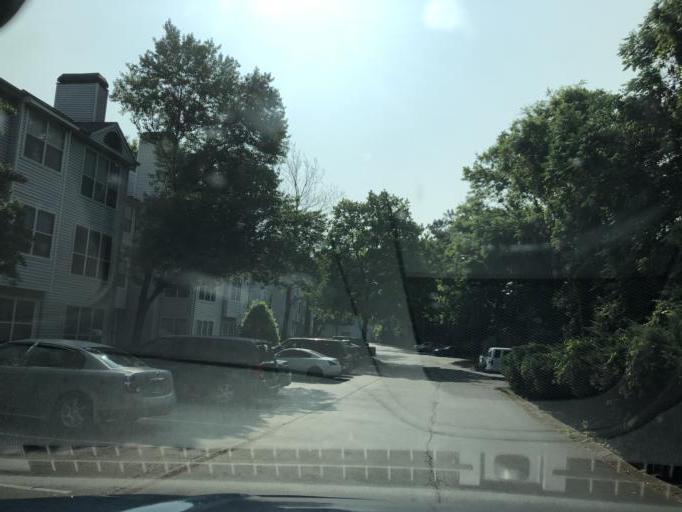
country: US
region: Tennessee
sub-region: Rutherford County
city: La Vergne
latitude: 36.0538
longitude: -86.6421
